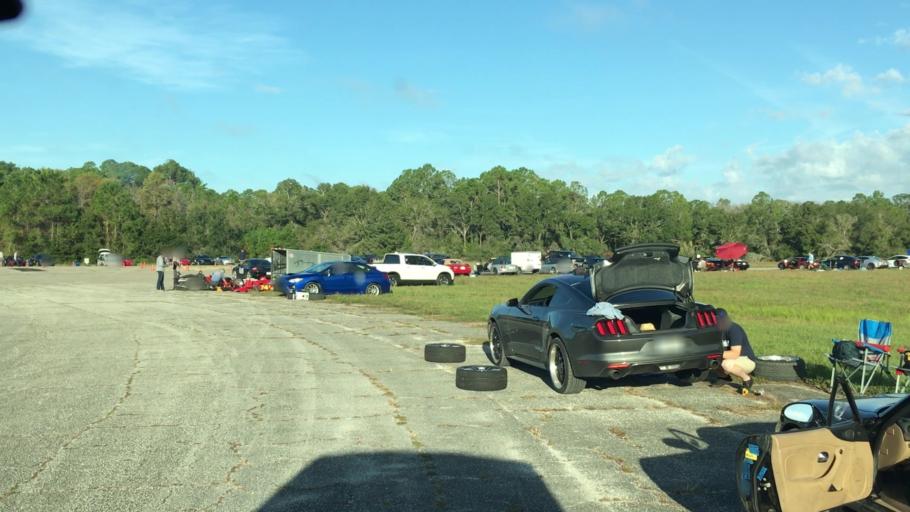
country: US
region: Florida
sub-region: Volusia County
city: North DeLand
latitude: 29.0764
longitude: -81.2860
